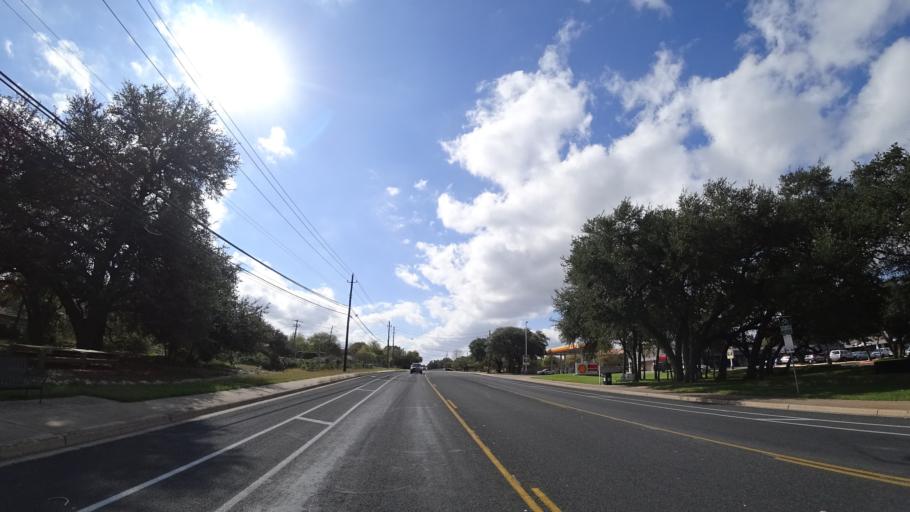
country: US
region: Texas
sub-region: Travis County
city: Wells Branch
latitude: 30.4214
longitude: -97.7157
